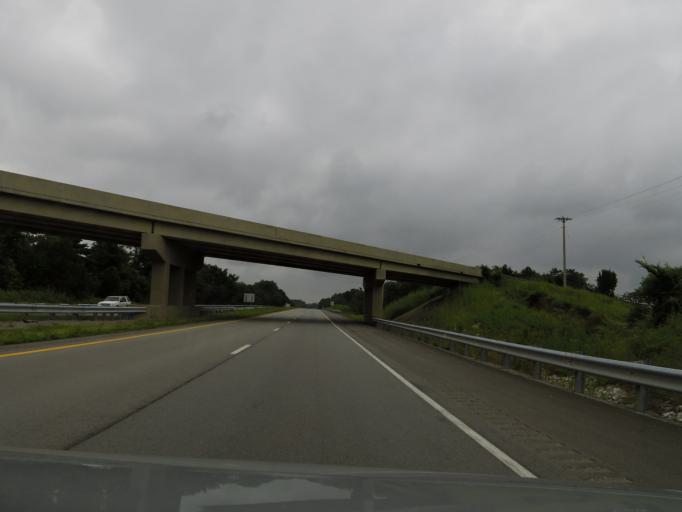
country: US
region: Kentucky
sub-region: Grayson County
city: Leitchfield
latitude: 37.4113
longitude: -86.4862
